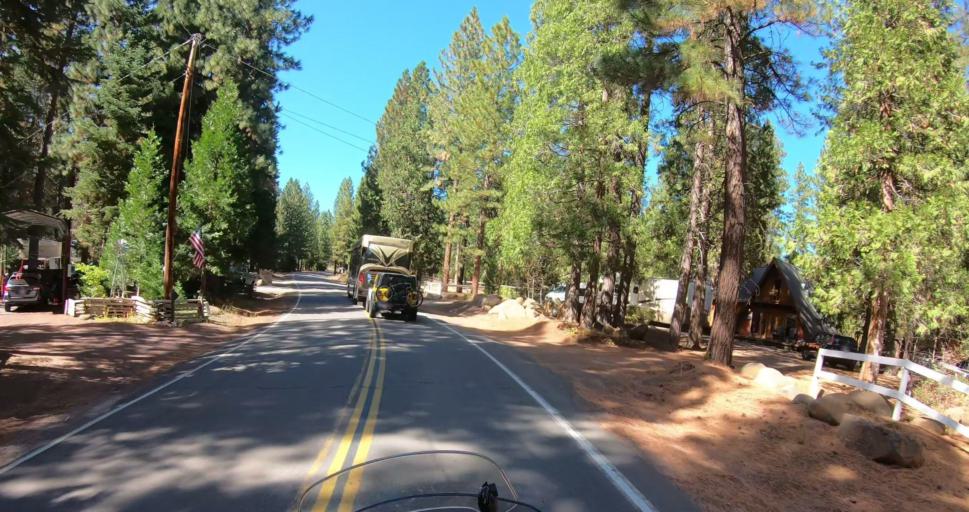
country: US
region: California
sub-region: Lassen County
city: Susanville
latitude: 40.4370
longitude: -120.7442
